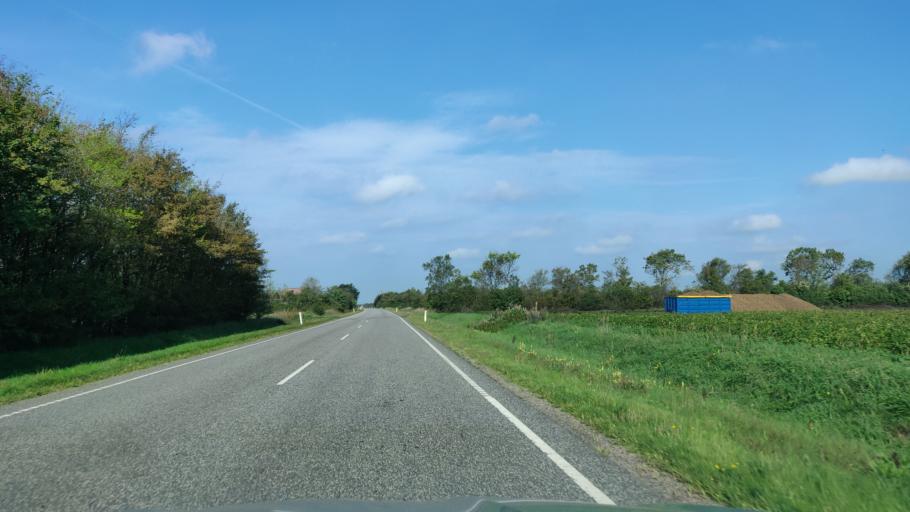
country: DK
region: Central Jutland
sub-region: Herning Kommune
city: Sunds
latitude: 56.2550
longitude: 9.0466
